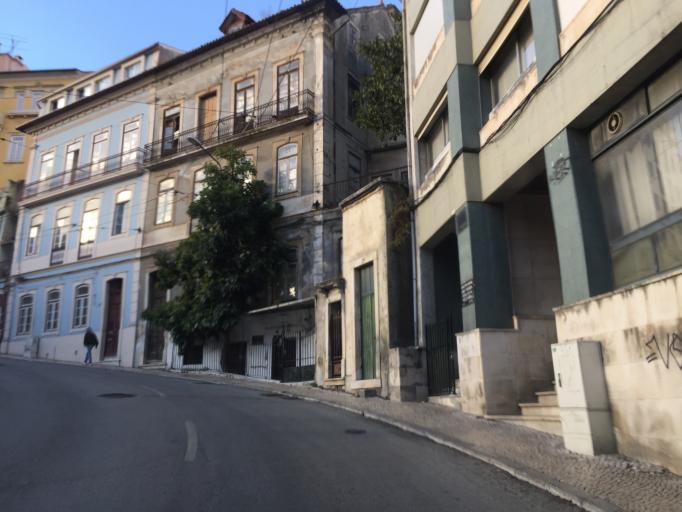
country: PT
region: Coimbra
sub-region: Coimbra
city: Coimbra
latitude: 40.2119
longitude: -8.4243
